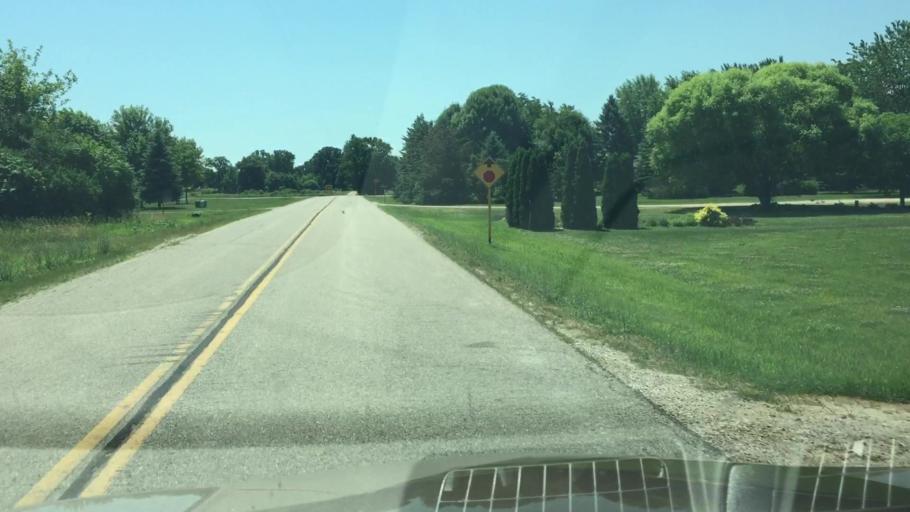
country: US
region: Wisconsin
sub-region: Fond du Lac County
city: Saint Peter
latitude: 43.9379
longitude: -88.3113
